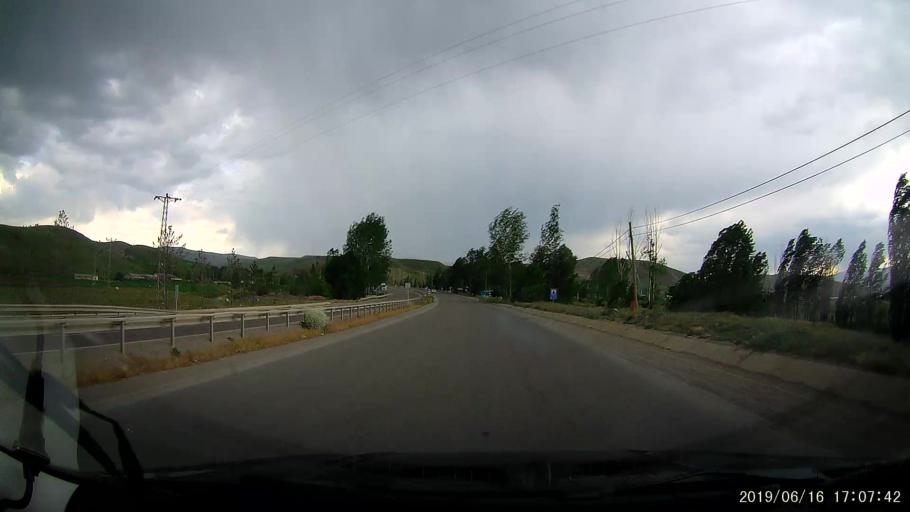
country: TR
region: Erzurum
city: Askale
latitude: 39.9167
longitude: 40.6707
